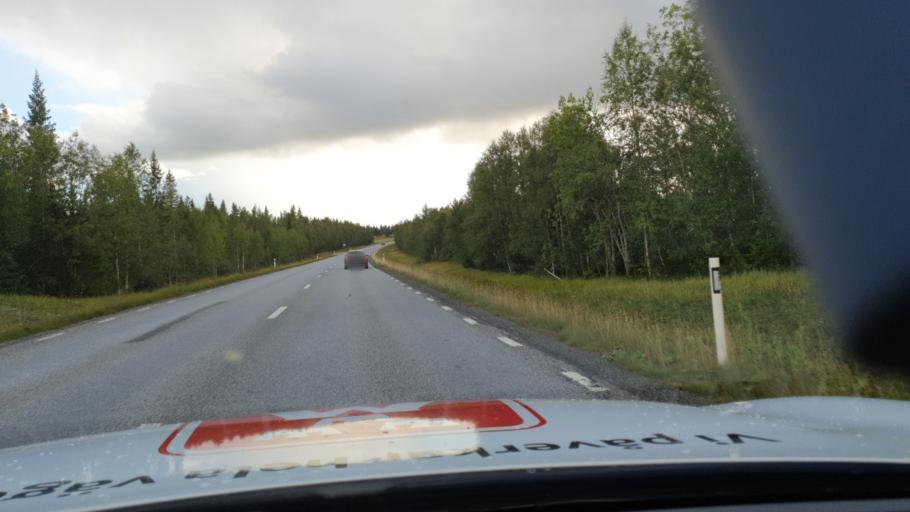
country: SE
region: Jaemtland
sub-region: OEstersunds Kommun
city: Lit
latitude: 63.4302
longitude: 15.1198
